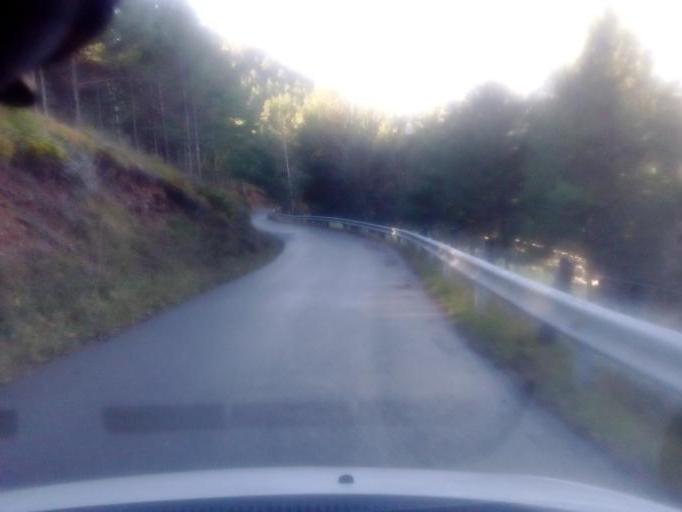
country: ES
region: Catalonia
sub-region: Provincia de Lleida
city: Bellver de Cerdanya
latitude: 42.3511
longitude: 1.7434
